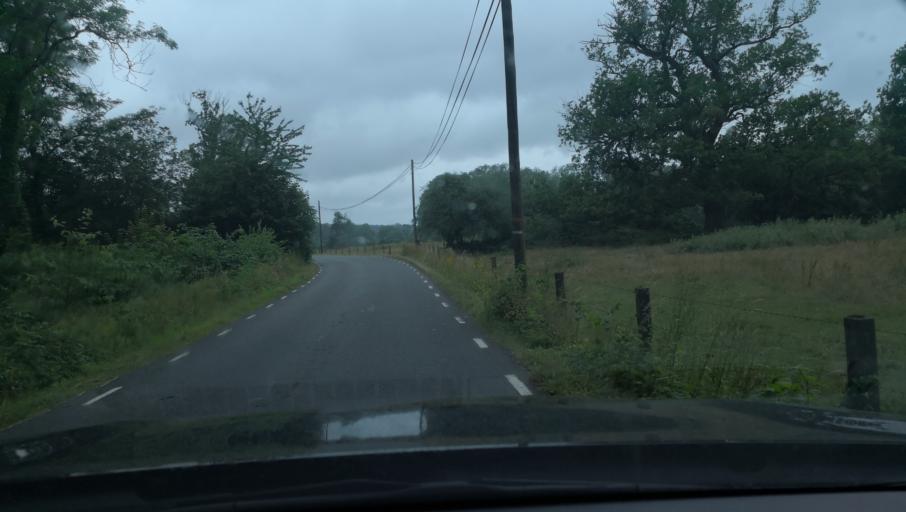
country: SE
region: Skane
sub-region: Simrishamns Kommun
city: Kivik
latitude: 55.6808
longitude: 14.2447
